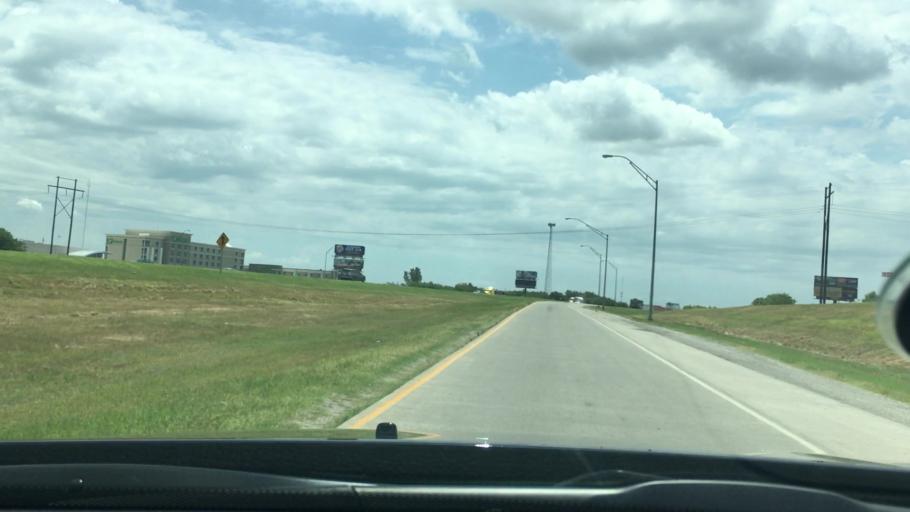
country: US
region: Oklahoma
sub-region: Carter County
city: Ardmore
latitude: 34.2008
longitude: -97.1649
